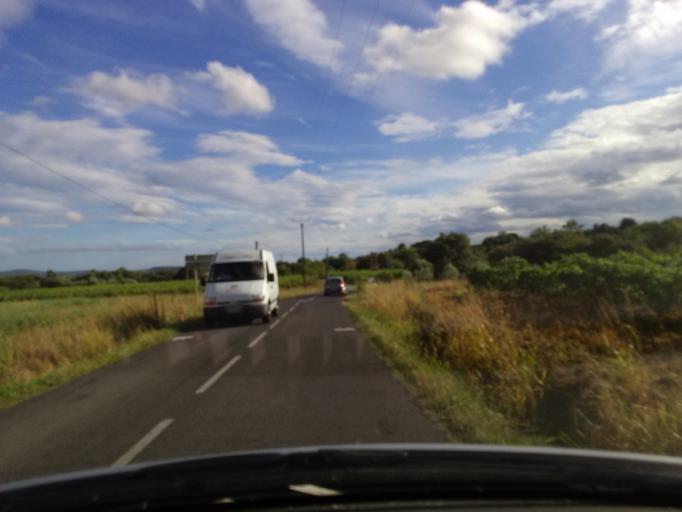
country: FR
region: Languedoc-Roussillon
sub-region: Departement de l'Herault
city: Montpeyroux
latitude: 43.6720
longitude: 3.5241
